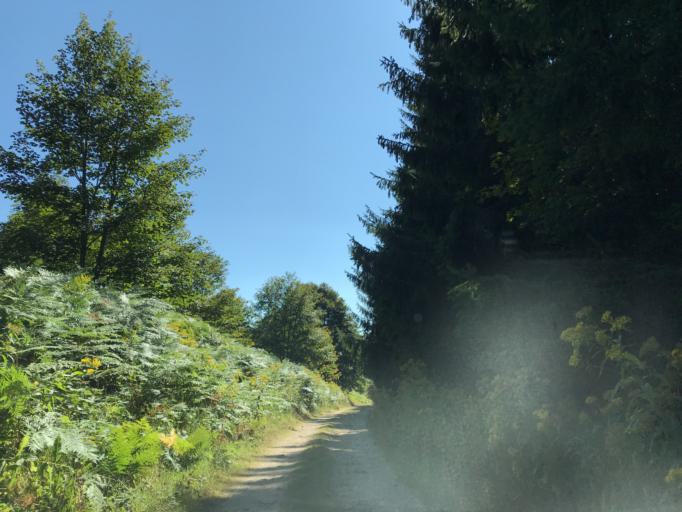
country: FR
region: Rhone-Alpes
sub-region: Departement de la Loire
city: Noiretable
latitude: 45.7635
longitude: 3.7510
